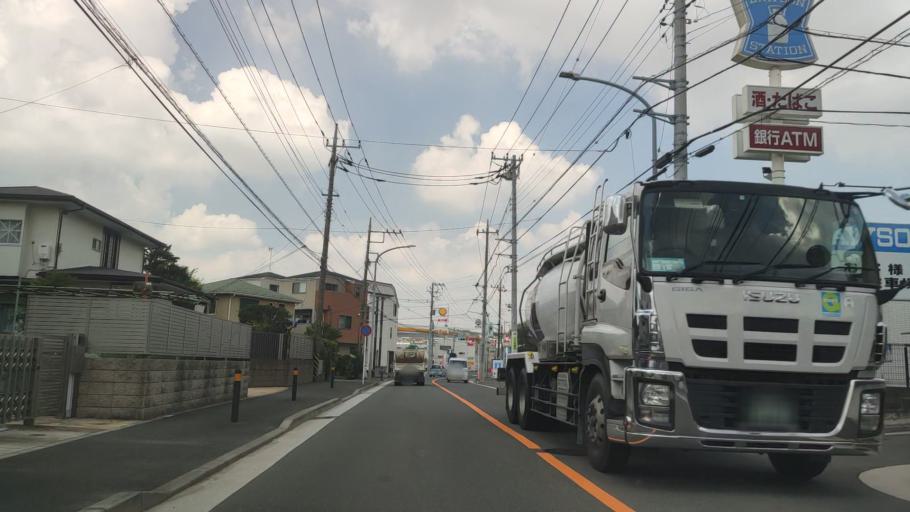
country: JP
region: Kanagawa
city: Minami-rinkan
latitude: 35.4291
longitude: 139.5150
